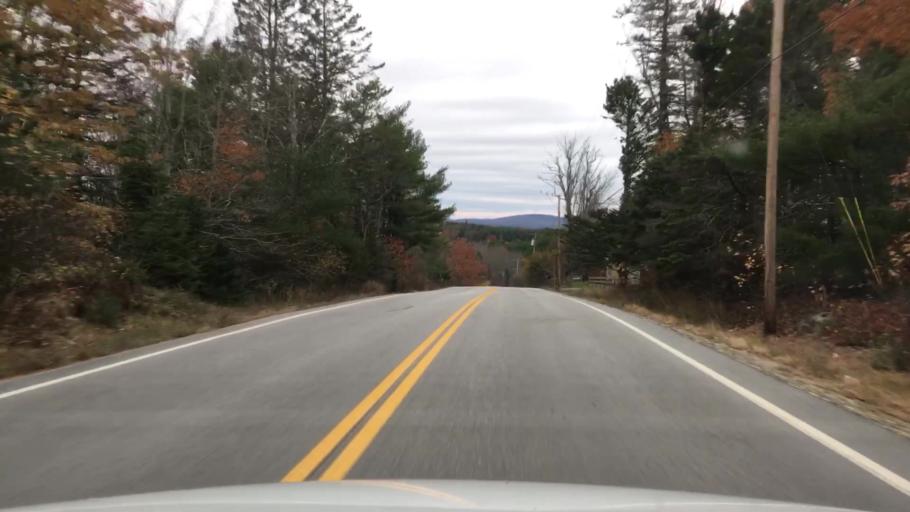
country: US
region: Maine
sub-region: Hancock County
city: Orland
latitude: 44.5355
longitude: -68.6784
